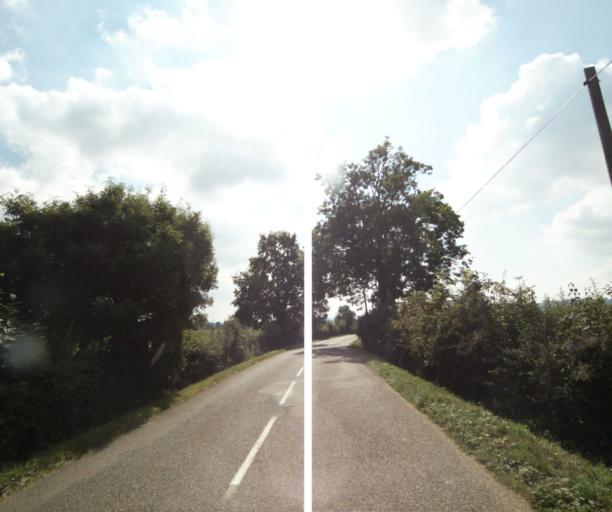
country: FR
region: Bourgogne
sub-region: Departement de Saone-et-Loire
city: Charolles
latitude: 46.3772
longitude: 4.2493
